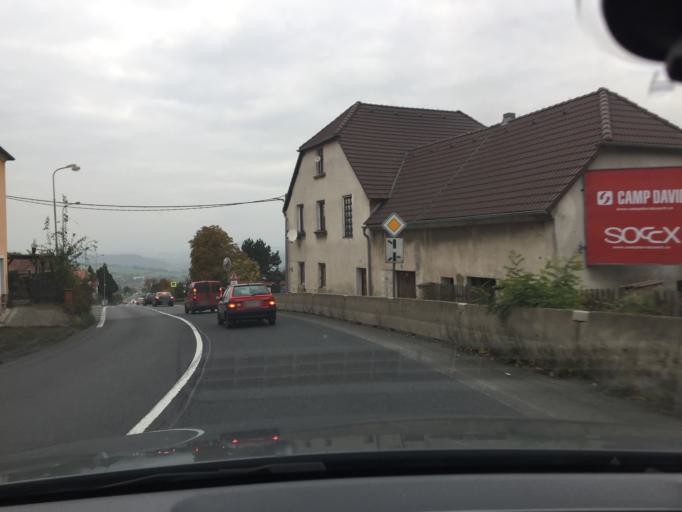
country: CZ
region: Ustecky
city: Rehlovice
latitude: 50.5795
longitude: 13.9293
